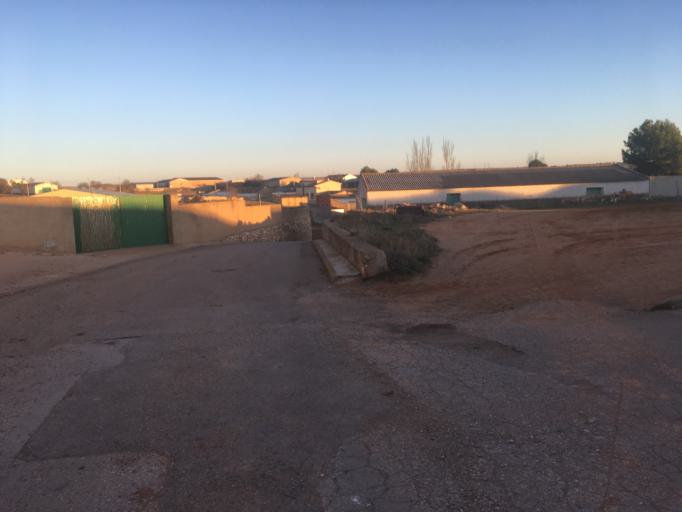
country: ES
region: Castille-La Mancha
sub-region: Provincia de Cuenca
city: Atalaya del Canavate
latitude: 39.5508
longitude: -2.2509
